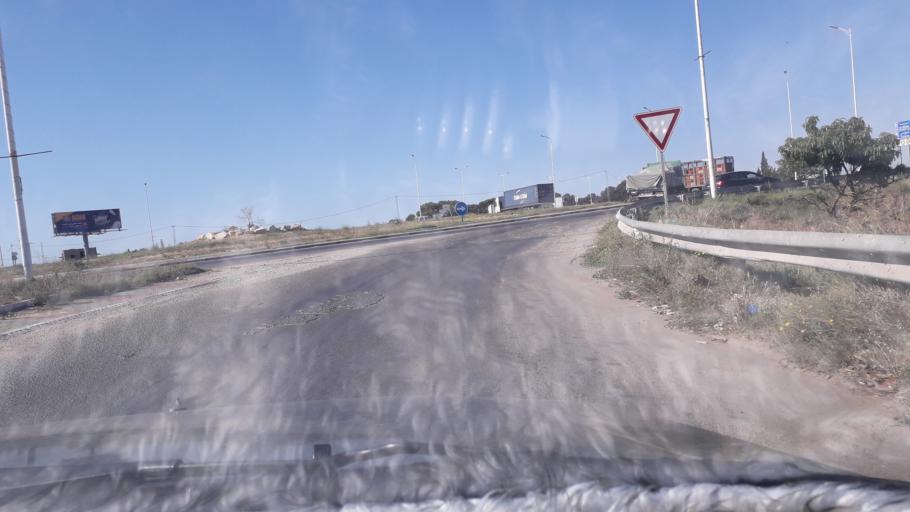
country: TN
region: Safaqis
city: Al Qarmadah
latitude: 34.8570
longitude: 10.7599
